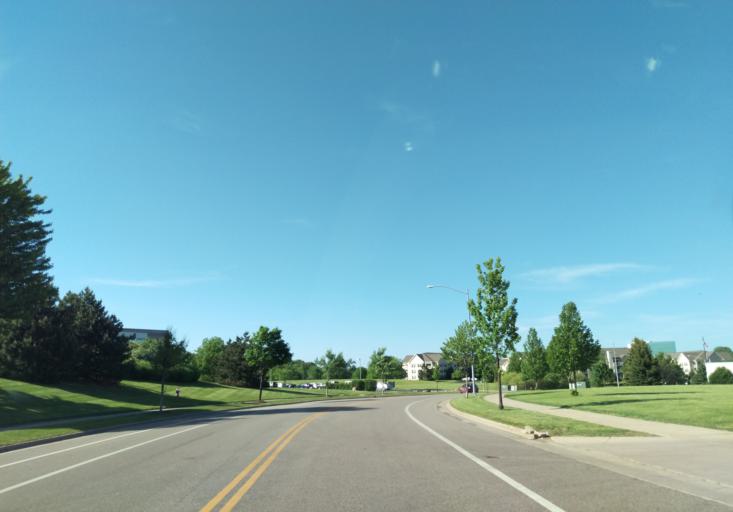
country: US
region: Wisconsin
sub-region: Dane County
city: Middleton
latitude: 43.0837
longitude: -89.5340
